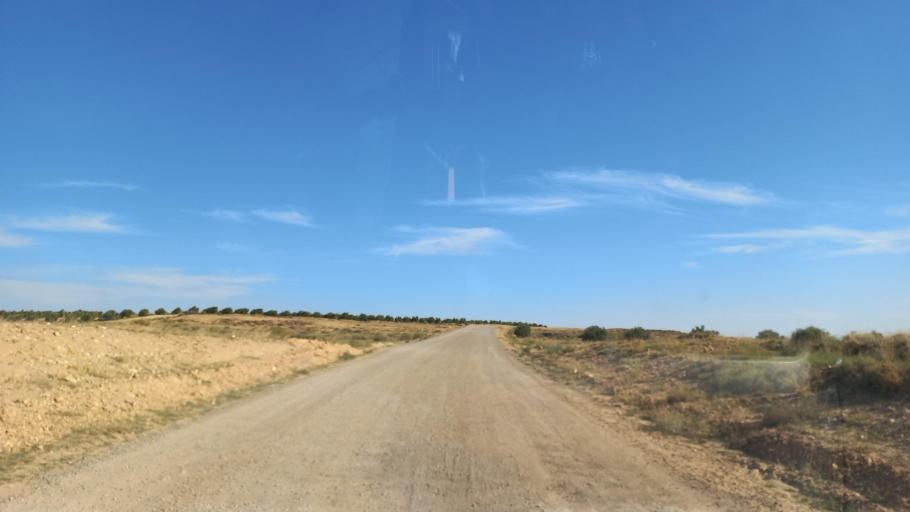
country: TN
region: Al Qasrayn
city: Sbiba
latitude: 35.3010
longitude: 9.0955
